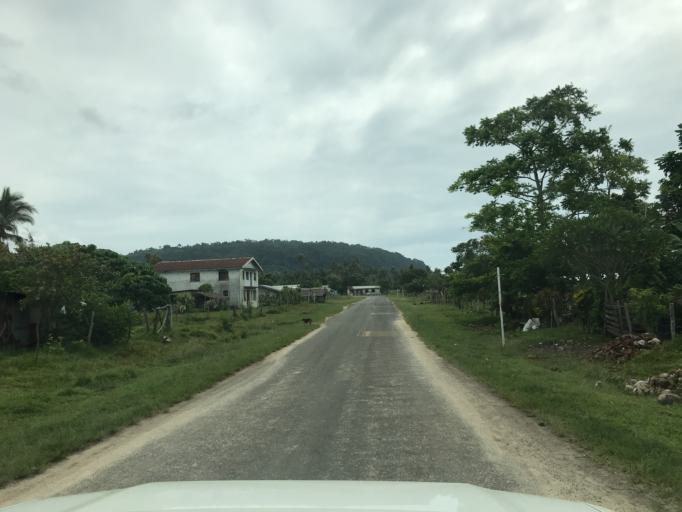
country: VU
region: Sanma
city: Port-Olry
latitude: -15.0441
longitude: 167.0720
